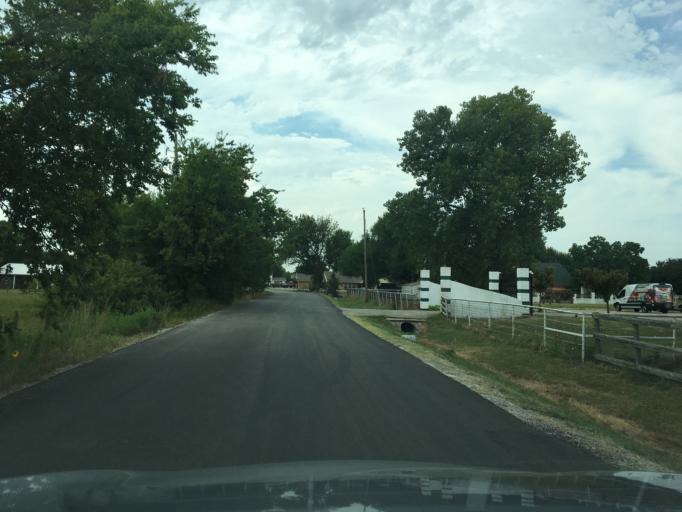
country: US
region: Texas
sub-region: Collin County
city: Parker
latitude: 33.0585
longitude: -96.6010
